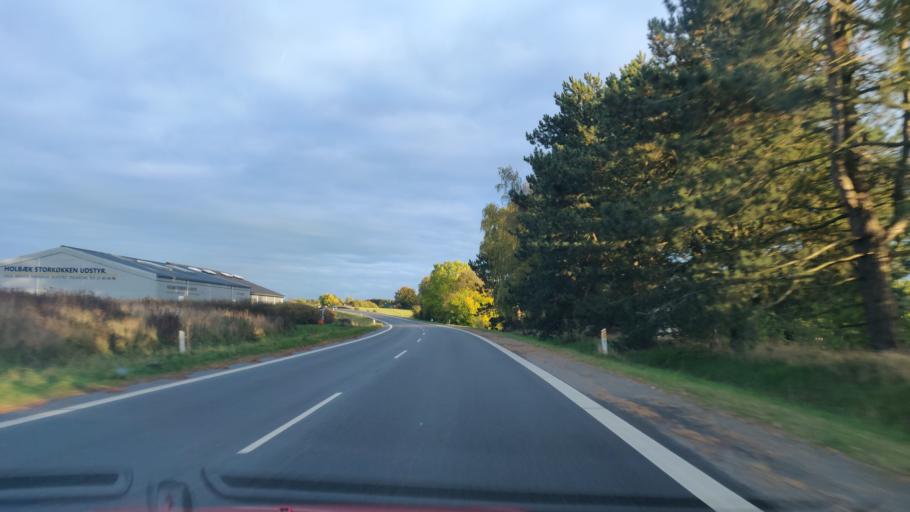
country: DK
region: Zealand
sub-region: Holbaek Kommune
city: Holbaek
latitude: 55.6863
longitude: 11.7008
